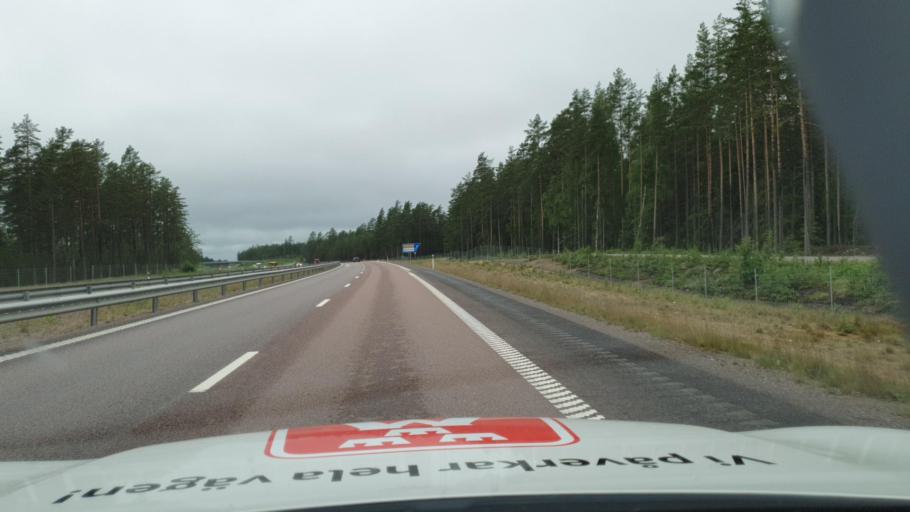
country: SE
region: Vaermland
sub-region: Kils Kommun
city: Kil
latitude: 59.3847
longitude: 13.3504
